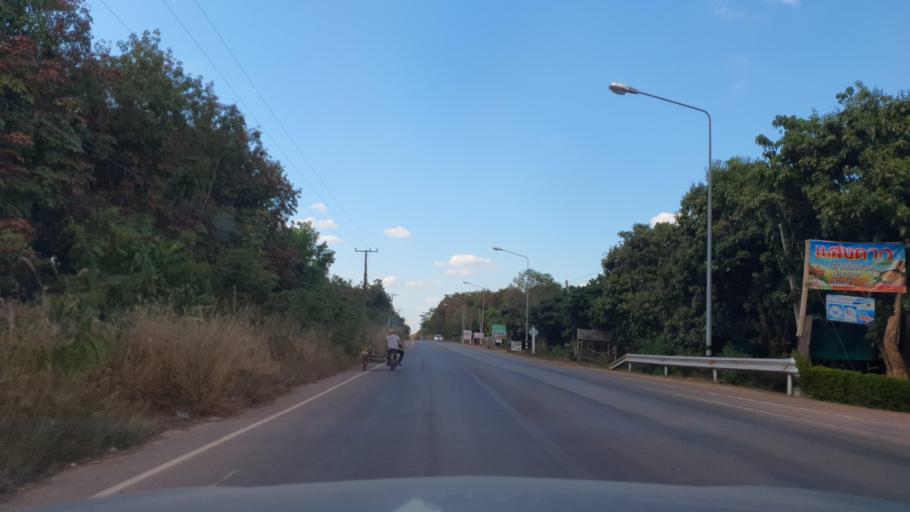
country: TH
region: Nong Khai
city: Bueng Khong Long
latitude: 17.9871
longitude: 104.0243
